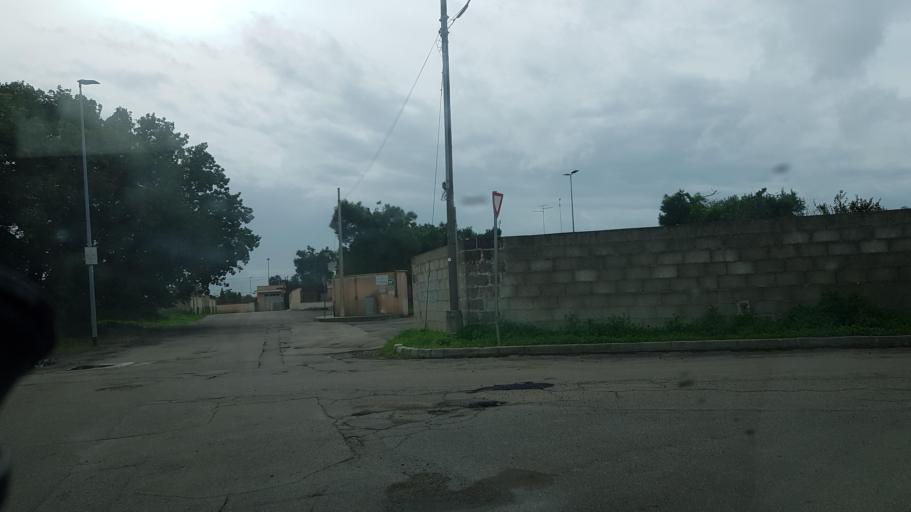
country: IT
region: Apulia
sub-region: Provincia di Lecce
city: Carmiano
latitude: 40.3420
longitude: 18.0515
